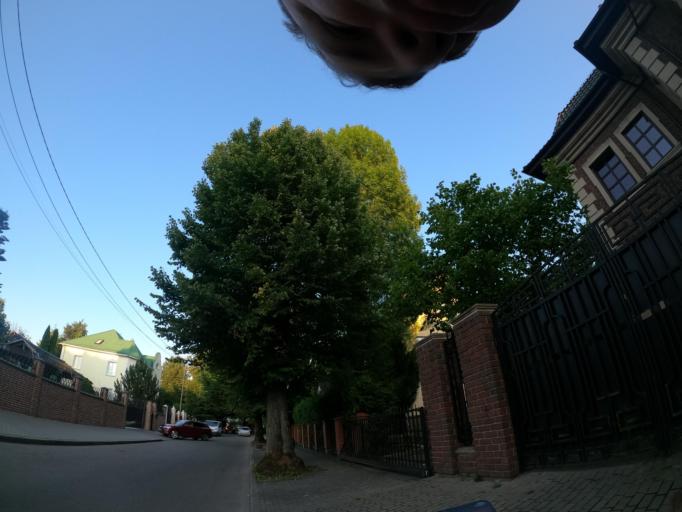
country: RU
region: Kaliningrad
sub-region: Gorod Kaliningrad
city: Kaliningrad
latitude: 54.7188
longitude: 20.4639
